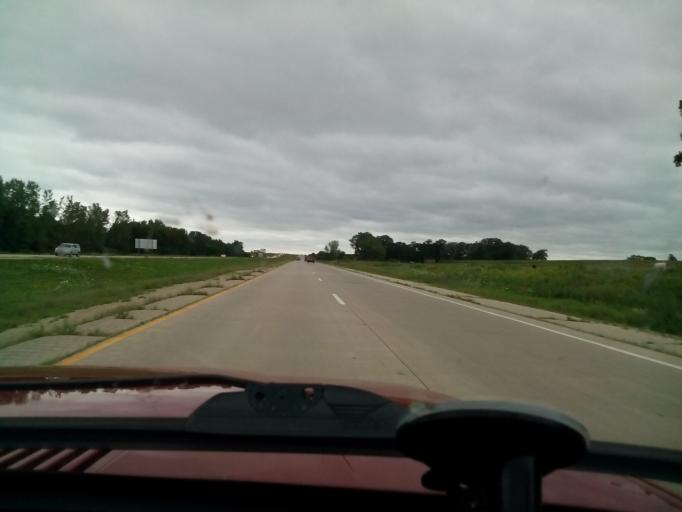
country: US
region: Wisconsin
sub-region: Columbia County
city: Columbus
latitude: 43.2996
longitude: -89.0585
